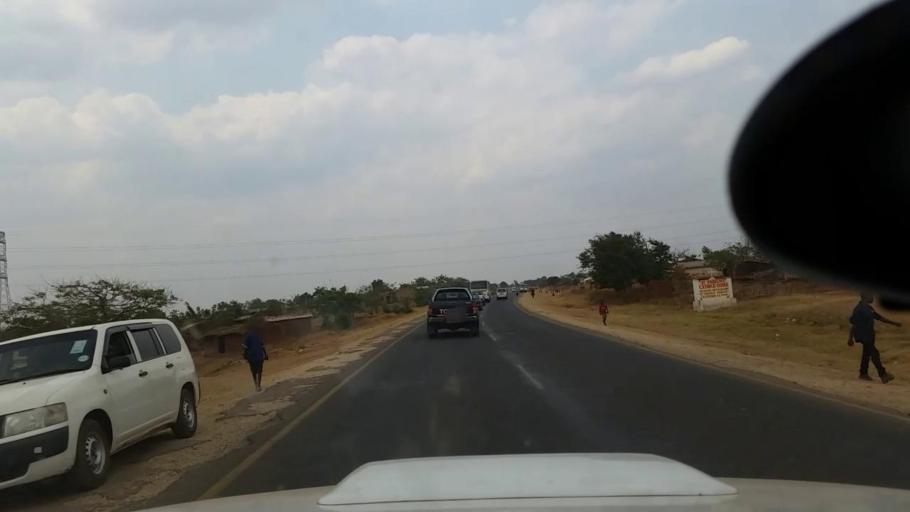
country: MW
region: Central Region
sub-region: Lilongwe District
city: Lilongwe
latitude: -13.8666
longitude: 33.8290
